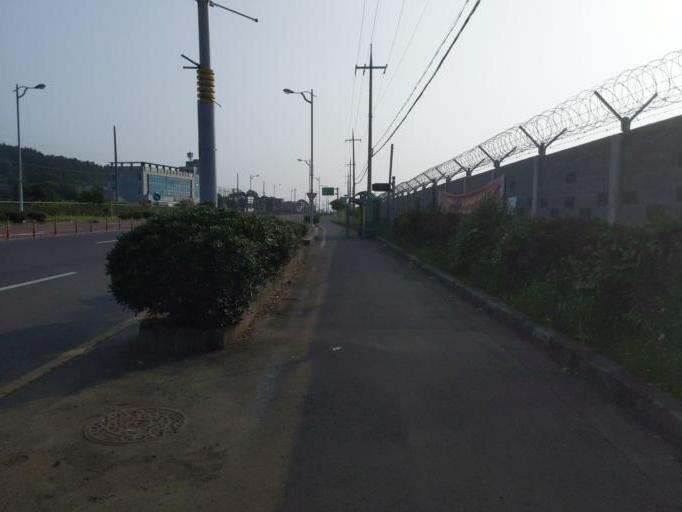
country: KR
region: Jeju-do
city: Gaigeturi
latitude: 33.2308
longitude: 126.2625
